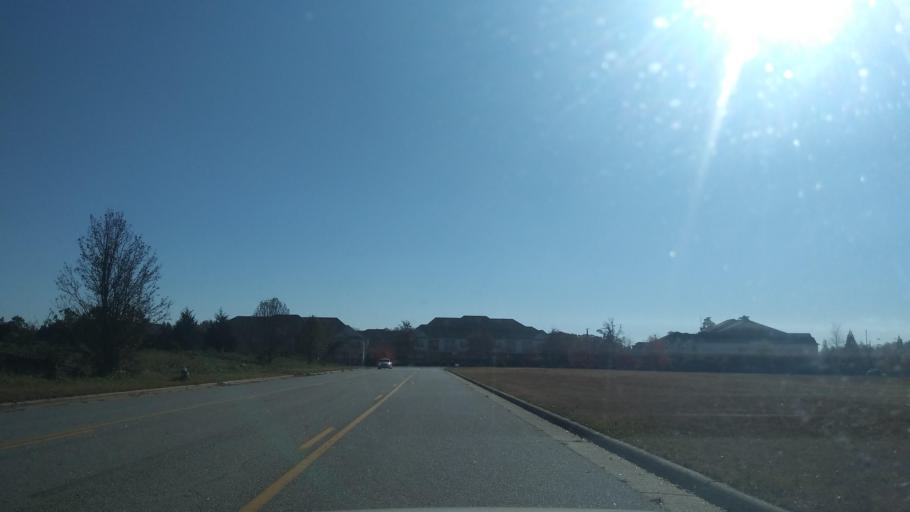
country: US
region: North Carolina
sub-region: Guilford County
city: Jamestown
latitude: 36.0482
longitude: -79.9003
